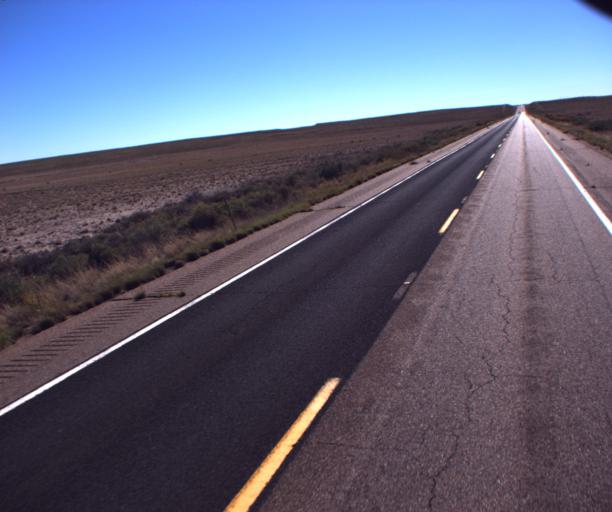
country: US
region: Arizona
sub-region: Navajo County
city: Snowflake
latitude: 34.7606
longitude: -109.8115
